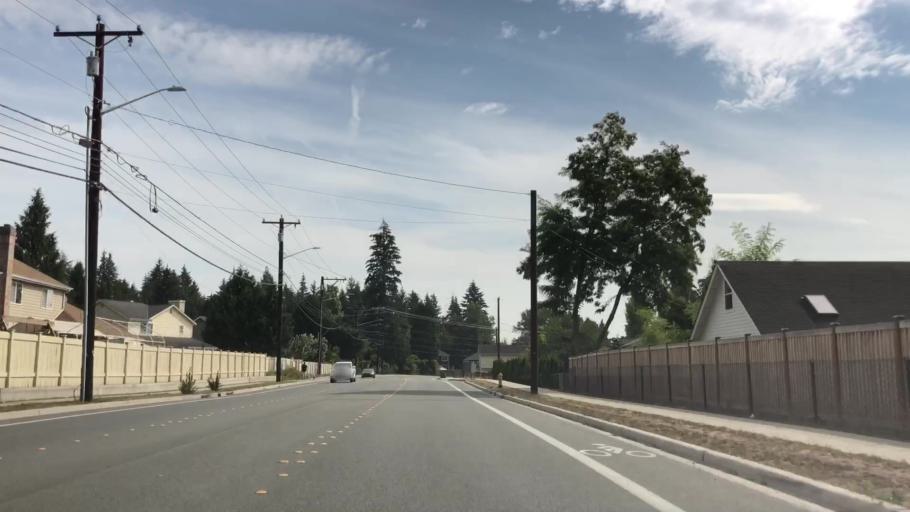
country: US
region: Washington
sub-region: Snohomish County
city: Martha Lake
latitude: 47.8404
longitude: -122.2357
